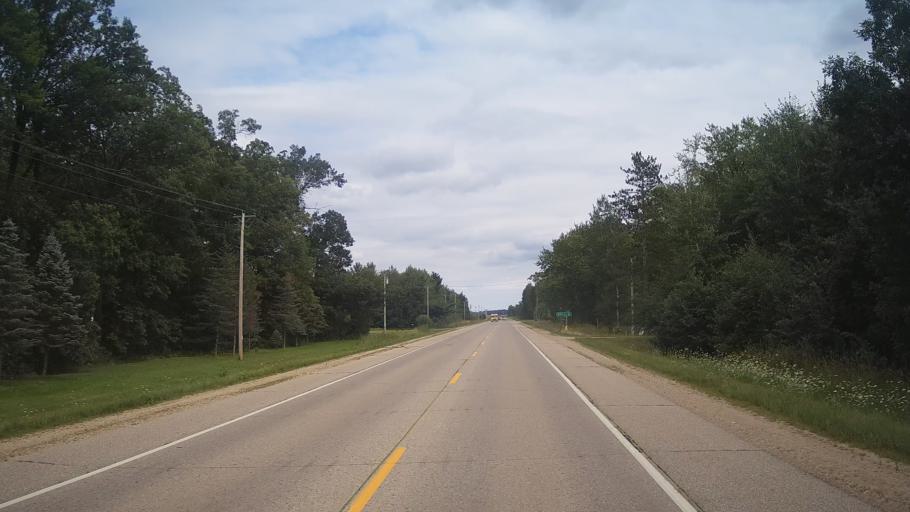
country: US
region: Wisconsin
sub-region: Waushara County
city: Redgranite
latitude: 44.0375
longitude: -89.0754
